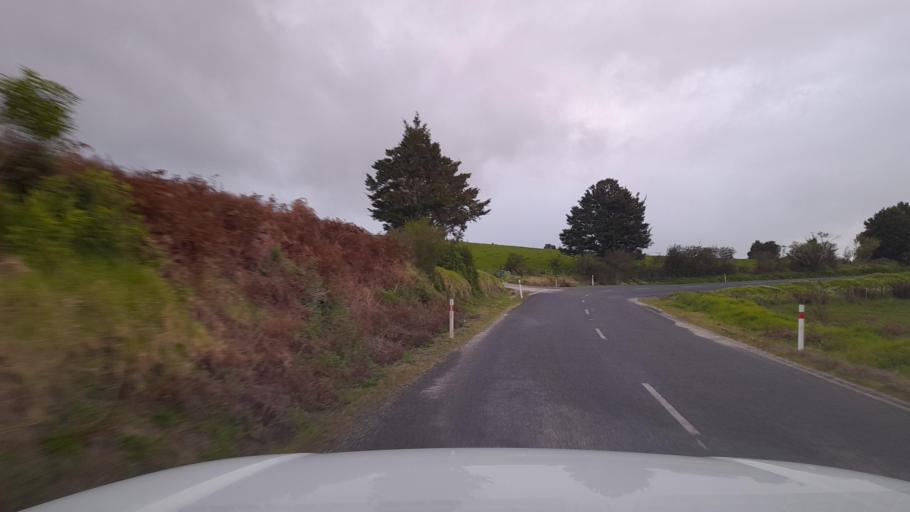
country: NZ
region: Northland
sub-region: Whangarei
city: Maungatapere
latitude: -35.6412
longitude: 174.2182
